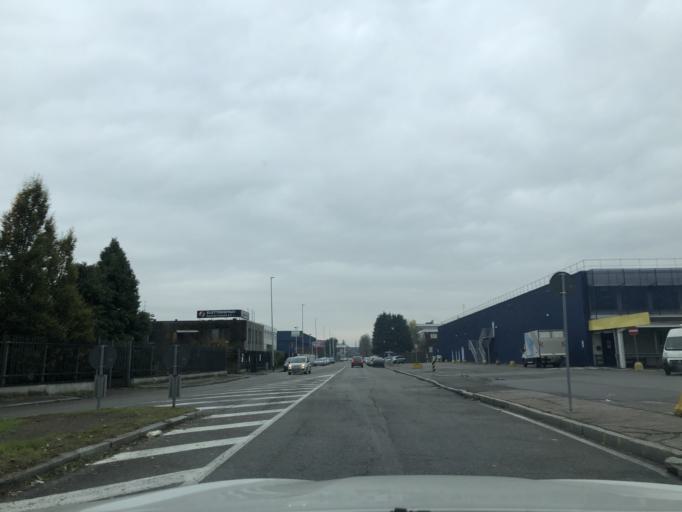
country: IT
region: Lombardy
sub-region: Citta metropolitana di Milano
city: Cesano Boscone
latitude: 45.4312
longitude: 9.0899
